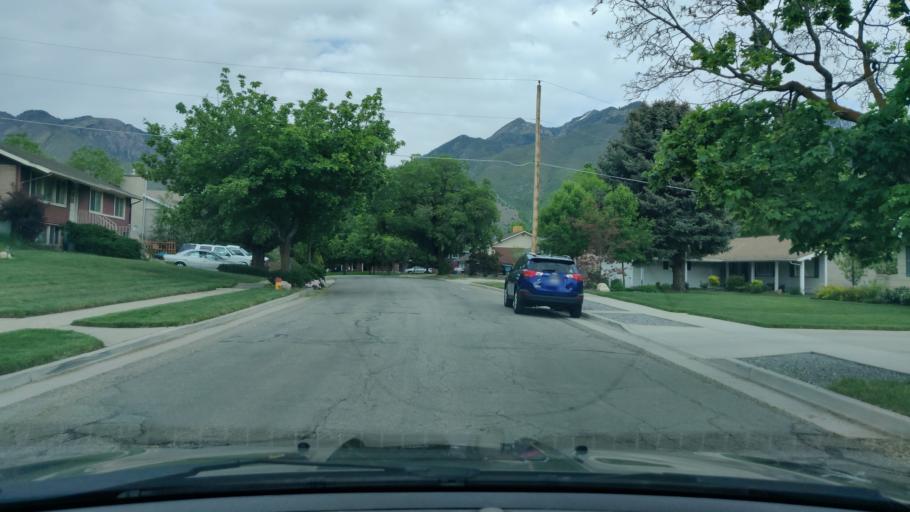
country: US
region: Utah
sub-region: Salt Lake County
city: Little Cottonwood Creek Valley
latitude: 40.6086
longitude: -111.8177
